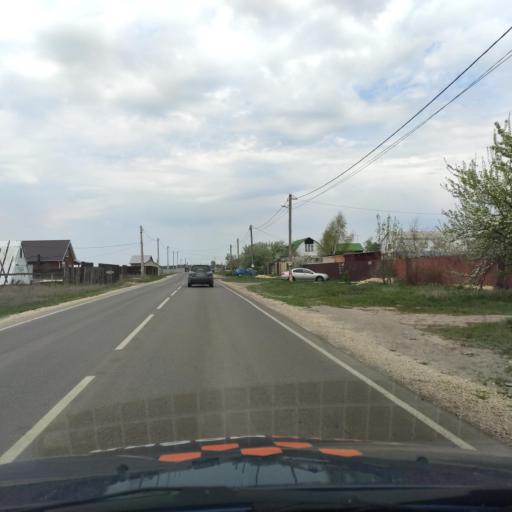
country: RU
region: Voronezj
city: Podgornoye
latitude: 51.8519
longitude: 39.1500
